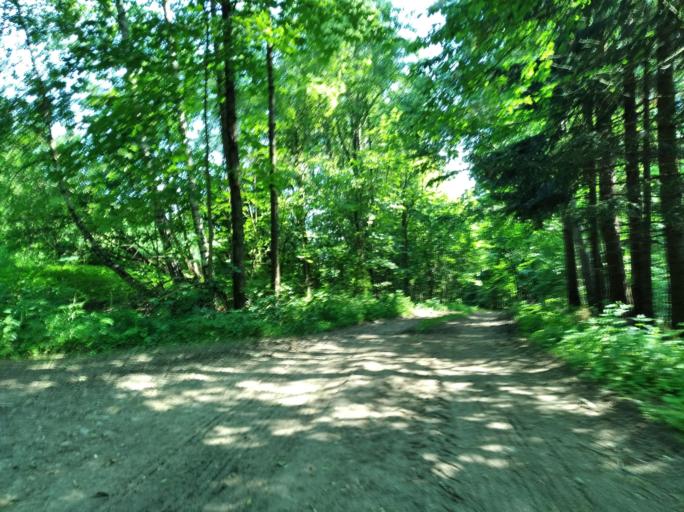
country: PL
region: Subcarpathian Voivodeship
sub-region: Powiat krosnienski
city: Odrzykon
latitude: 49.7681
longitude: 21.7522
